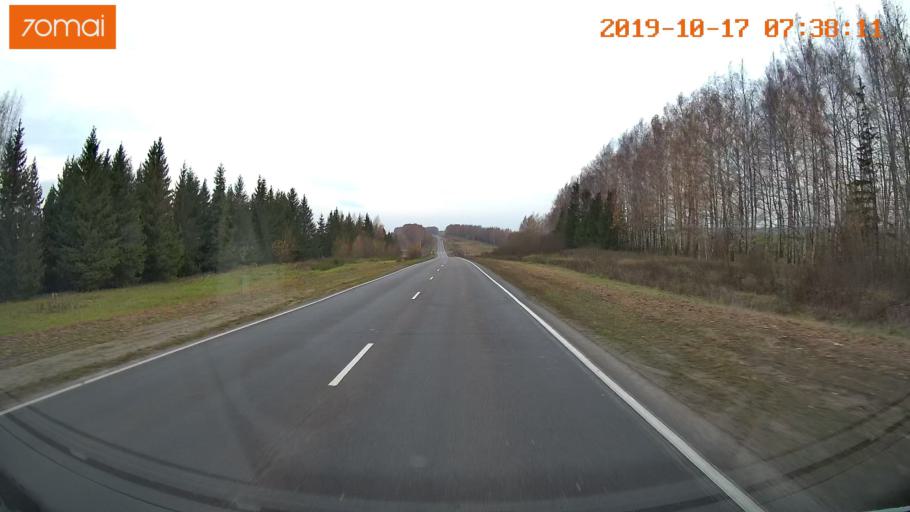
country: RU
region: Vladimir
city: Yur'yev-Pol'skiy
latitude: 56.4537
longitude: 39.8807
